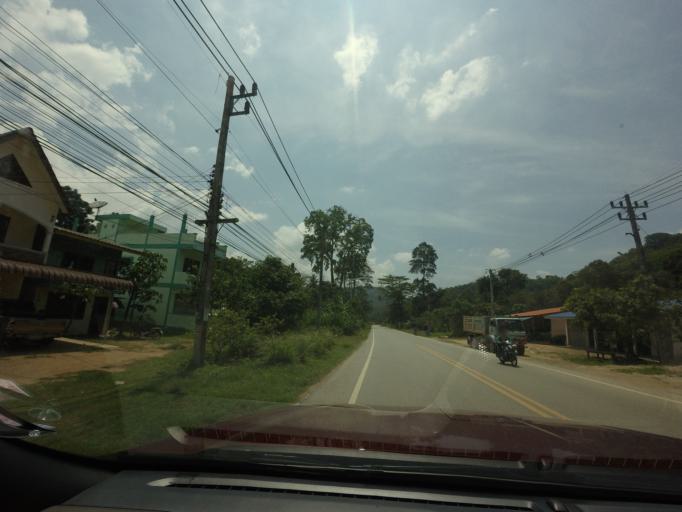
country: TH
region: Yala
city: Betong
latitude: 5.8108
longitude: 101.0835
